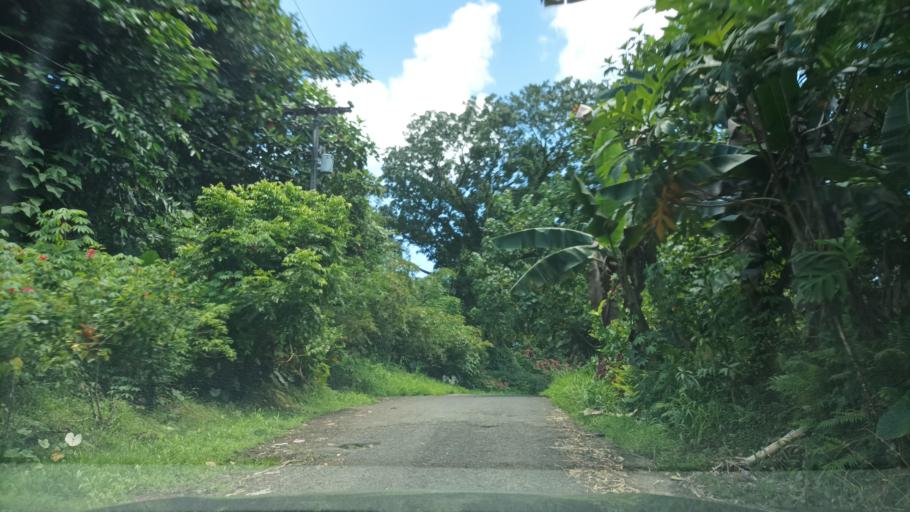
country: FM
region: Pohnpei
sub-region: Madolenihm Municipality
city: Madolenihm Municipality Government
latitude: 6.8459
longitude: 158.3037
